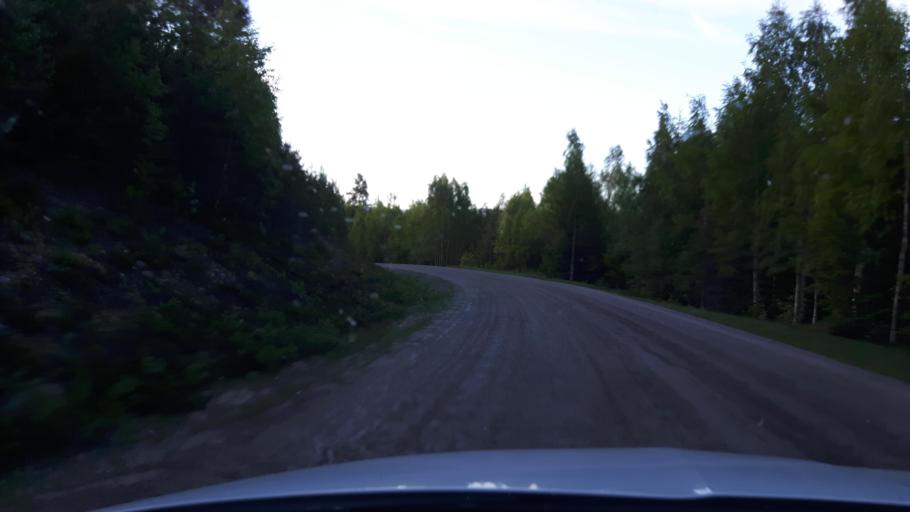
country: SE
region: Gaevleborg
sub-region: Ljusdals Kommun
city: Farila
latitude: 62.0085
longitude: 15.8363
